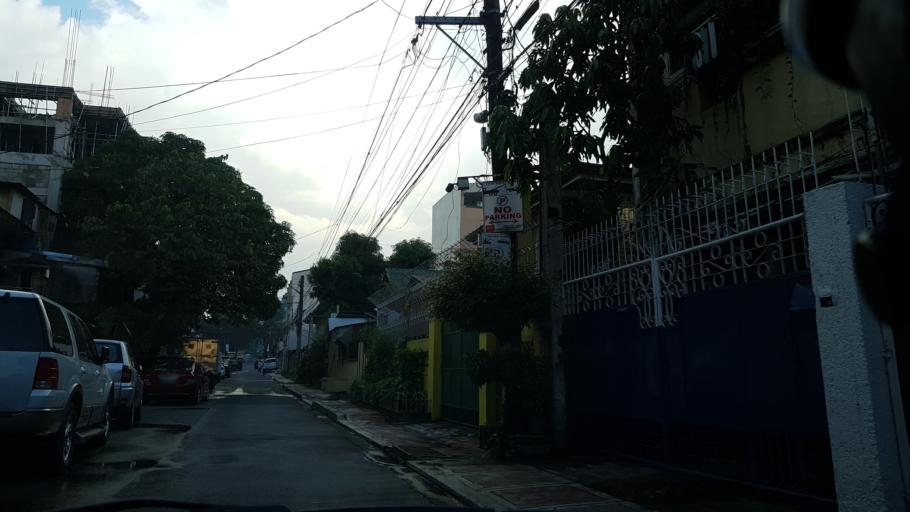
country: PH
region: Metro Manila
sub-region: Quezon City
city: Quezon City
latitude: 14.6335
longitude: 121.0574
